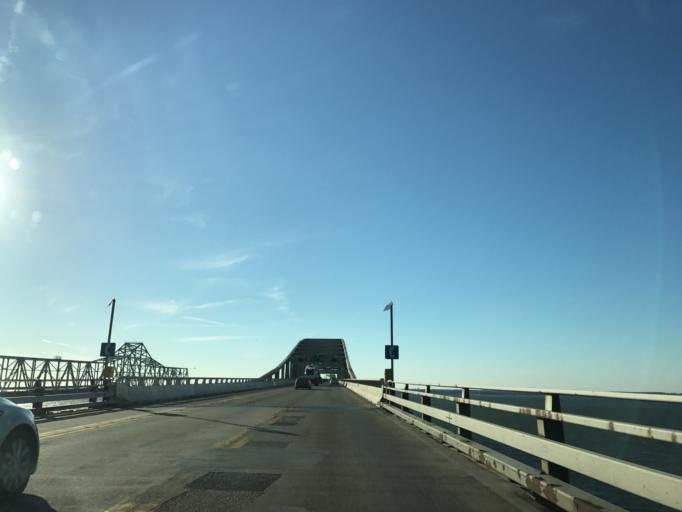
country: US
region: Maryland
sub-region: Queen Anne's County
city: Stevensville
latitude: 38.9881
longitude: -76.3548
